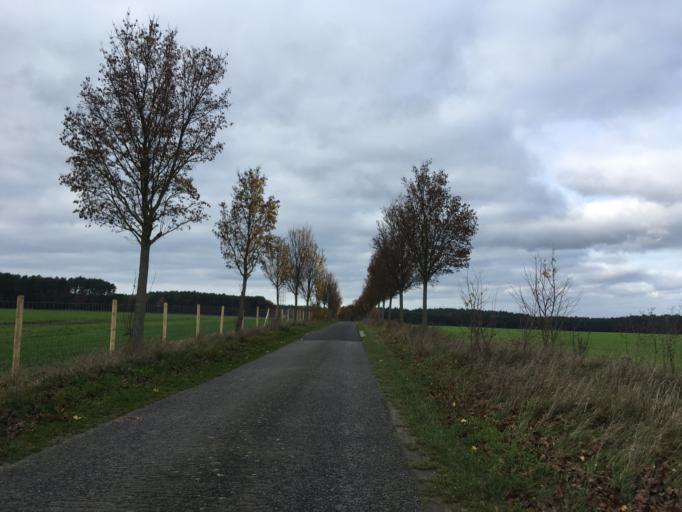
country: DE
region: Brandenburg
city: Schenkendobern
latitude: 51.9837
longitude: 14.5285
